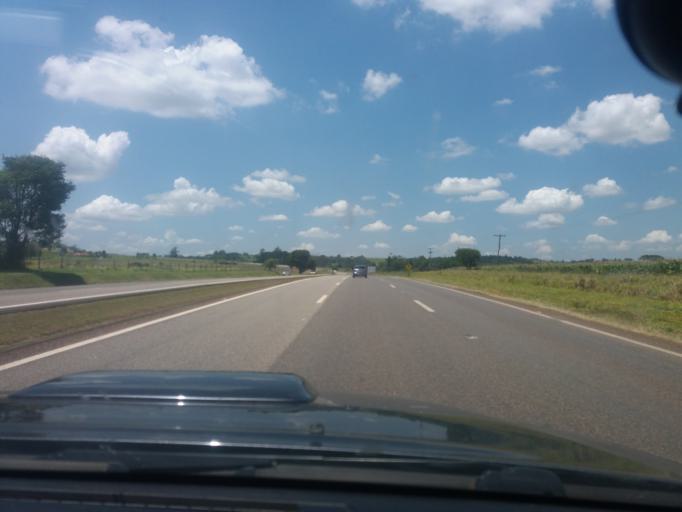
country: BR
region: Sao Paulo
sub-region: Itapetininga
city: Itapetininga
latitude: -23.4762
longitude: -47.9717
